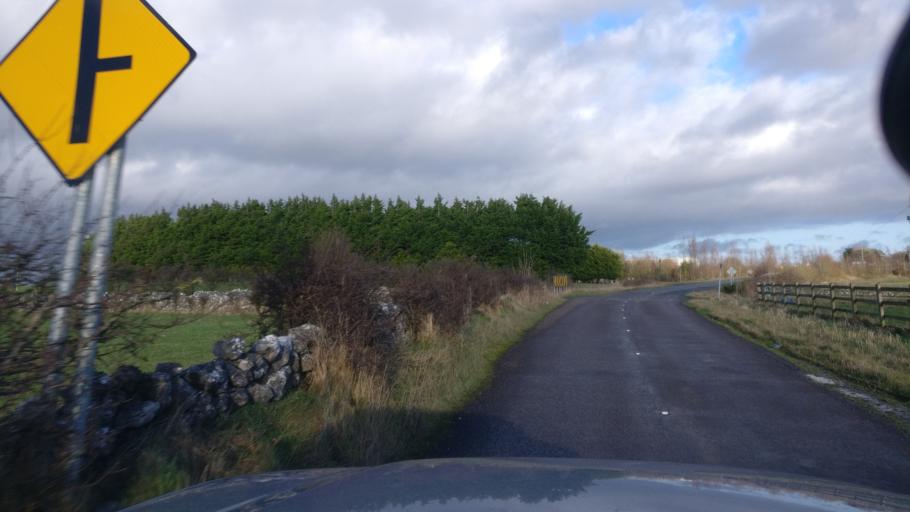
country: IE
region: Connaught
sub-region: County Galway
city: Loughrea
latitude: 53.2617
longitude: -8.6117
